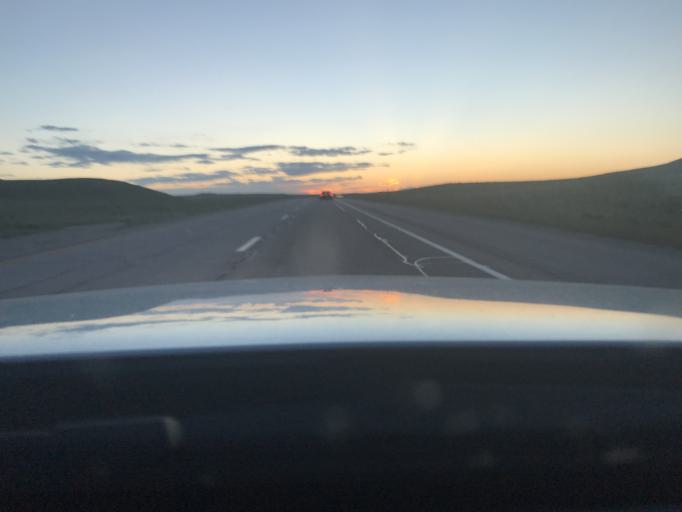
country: US
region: Wyoming
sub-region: Converse County
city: Glenrock
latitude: 42.8347
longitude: -105.8493
